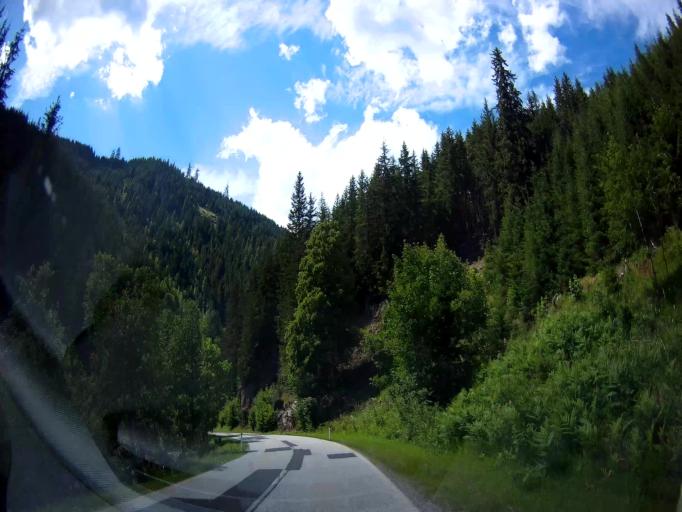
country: AT
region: Styria
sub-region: Politischer Bezirk Murau
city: Stadl an der Mur
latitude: 47.0378
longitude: 14.0037
